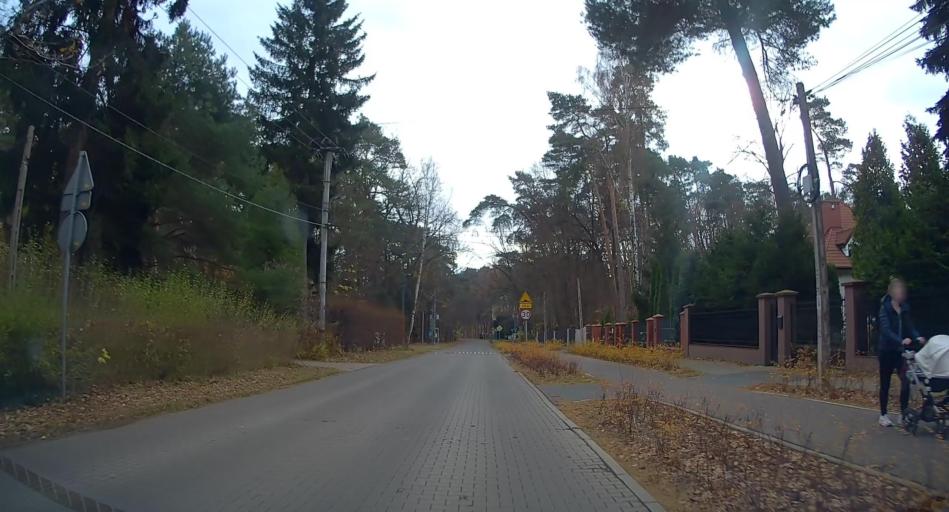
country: PL
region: Masovian Voivodeship
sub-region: Powiat piaseczynski
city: Piaseczno
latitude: 52.0561
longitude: 21.0186
